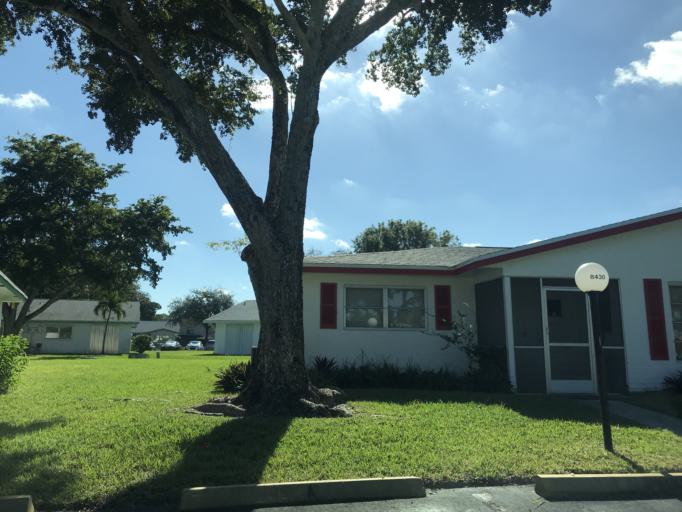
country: US
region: Florida
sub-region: Broward County
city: Plantation
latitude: 26.1368
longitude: -80.2620
